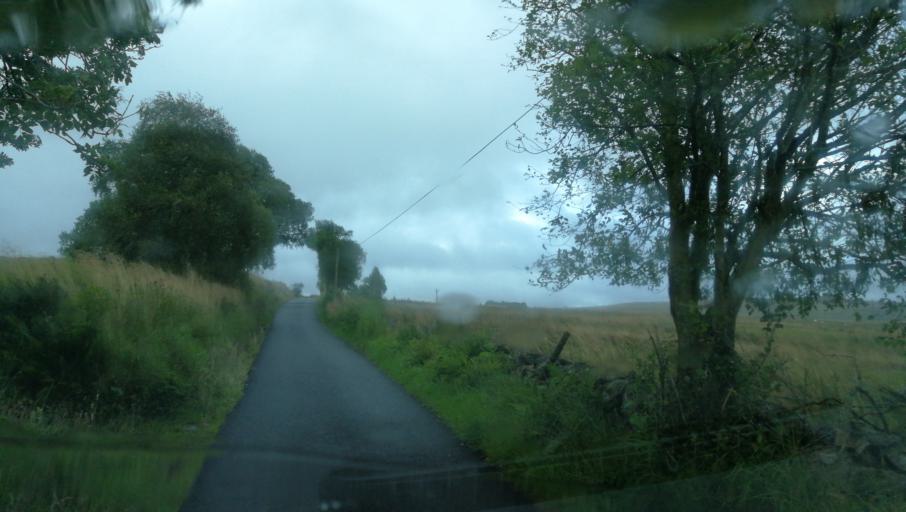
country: GB
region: Scotland
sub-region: Perth and Kinross
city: Blairgowrie
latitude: 56.6901
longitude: -3.3980
